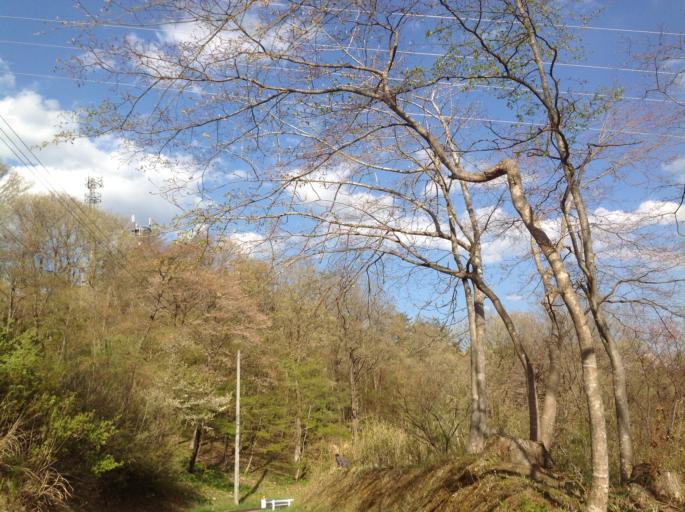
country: JP
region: Iwate
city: Ichinoseki
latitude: 38.9437
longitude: 141.1196
